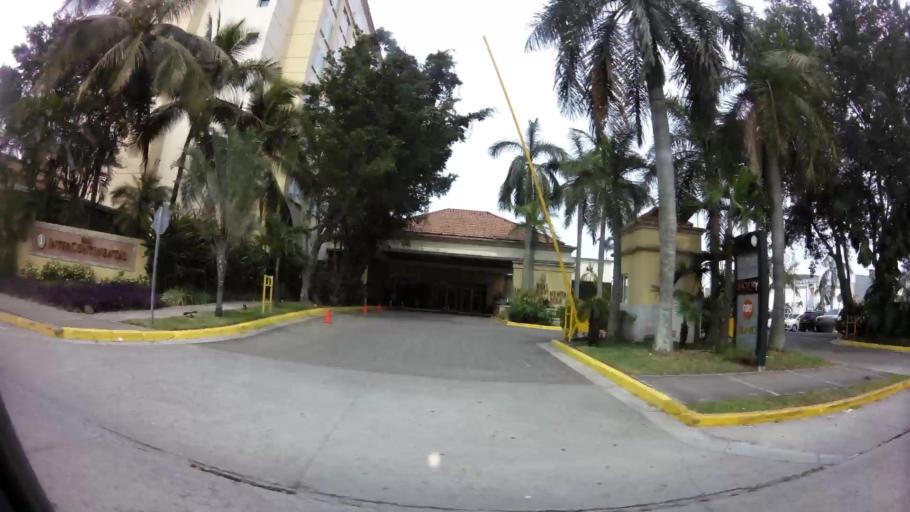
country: HN
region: Cortes
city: San Pedro Sula
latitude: 15.4946
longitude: -88.0351
